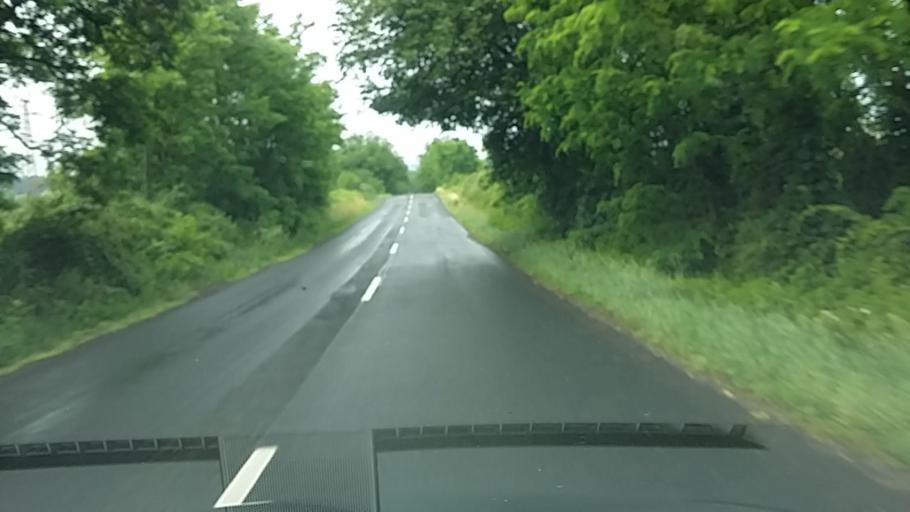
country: SK
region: Nitriansky
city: Sahy
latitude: 47.9883
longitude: 18.8179
